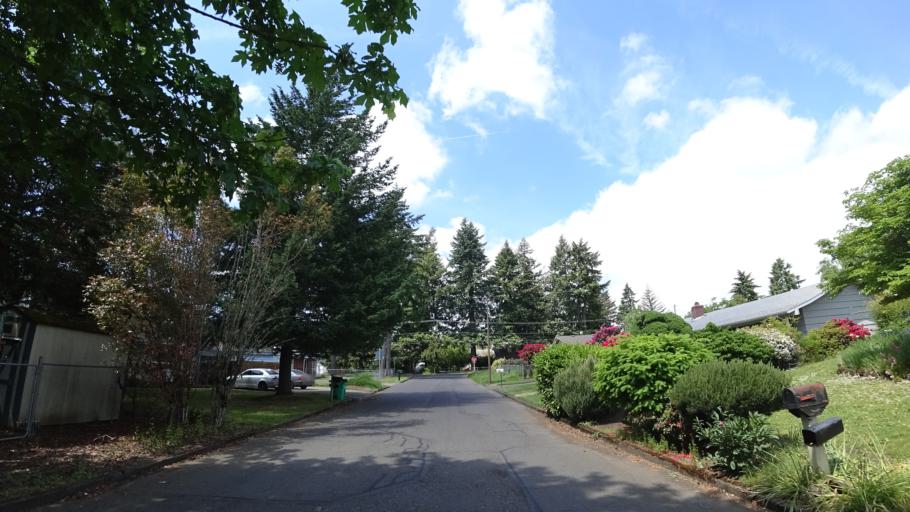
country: US
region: Oregon
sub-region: Multnomah County
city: Gresham
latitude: 45.5005
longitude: -122.4942
